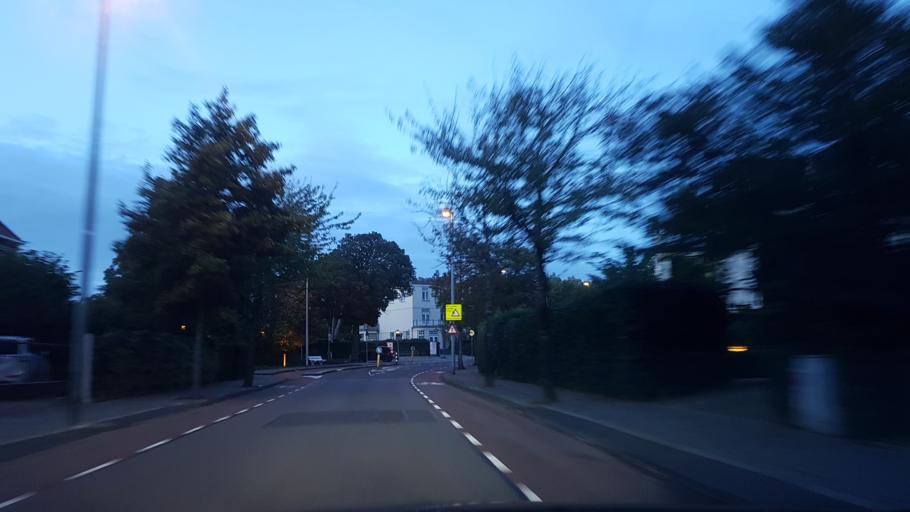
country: NL
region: North Holland
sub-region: Gemeente Zandvoort
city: Zandvoort
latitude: 52.3701
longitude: 4.5398
